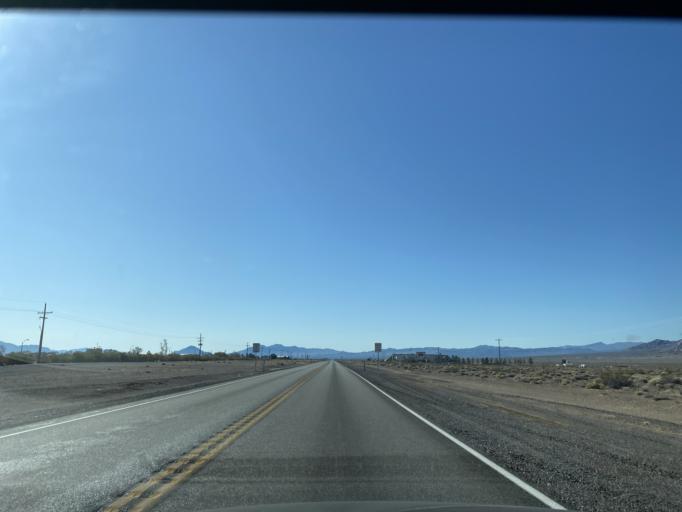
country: US
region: Nevada
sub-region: Nye County
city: Pahrump
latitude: 36.4199
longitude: -116.4223
